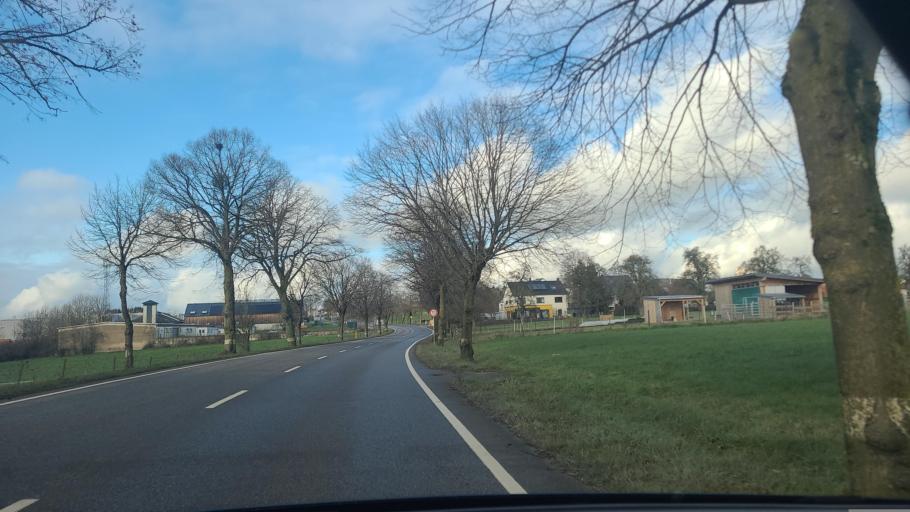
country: LU
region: Luxembourg
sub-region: Canton de Capellen
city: Dippach
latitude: 49.5828
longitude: 5.9788
